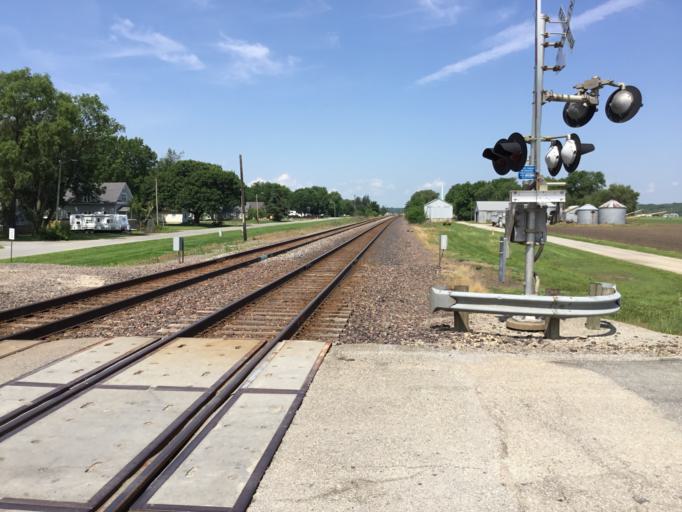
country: US
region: Kansas
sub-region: Shawnee County
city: Topeka
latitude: 39.0839
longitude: -95.5577
